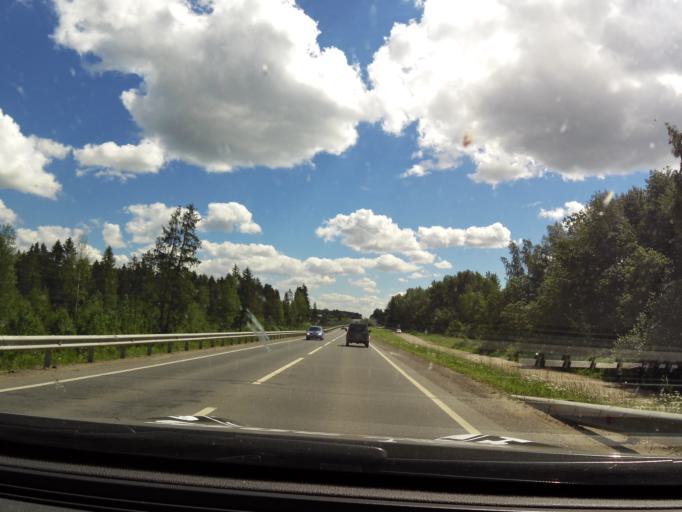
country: RU
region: Vologda
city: Molochnoye
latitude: 59.2834
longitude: 39.7006
